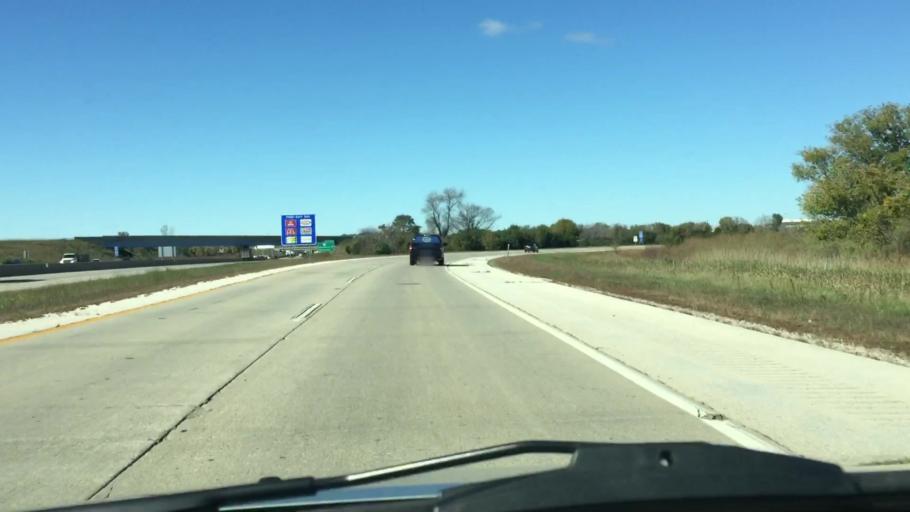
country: US
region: Wisconsin
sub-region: Waukesha County
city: Pewaukee
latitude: 43.0480
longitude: -88.2451
